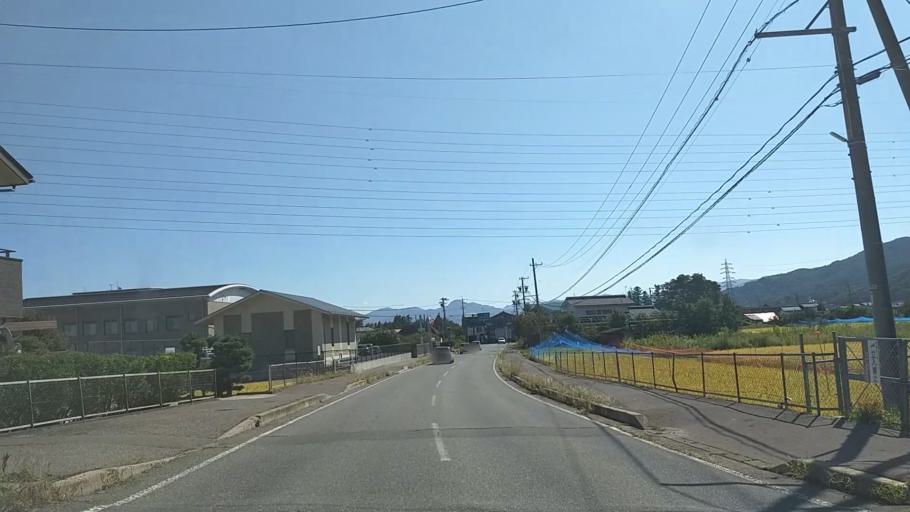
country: JP
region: Nagano
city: Nagano-shi
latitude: 36.6181
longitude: 138.1417
